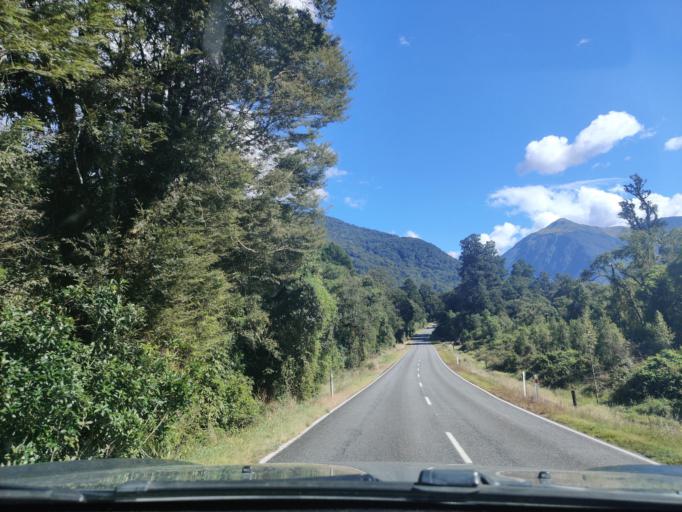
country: NZ
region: Otago
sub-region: Queenstown-Lakes District
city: Wanaka
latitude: -43.9723
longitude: 169.3860
